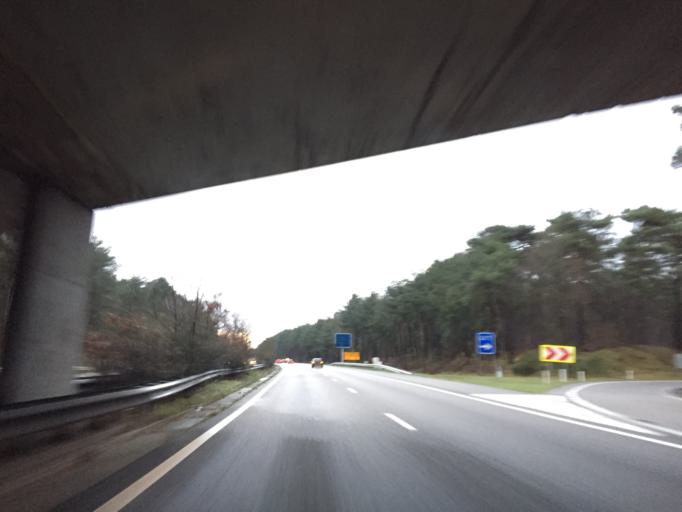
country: NL
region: North Brabant
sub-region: Gemeente Bergen op Zoom
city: Bergen op Zoom
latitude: 51.4789
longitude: 4.3158
